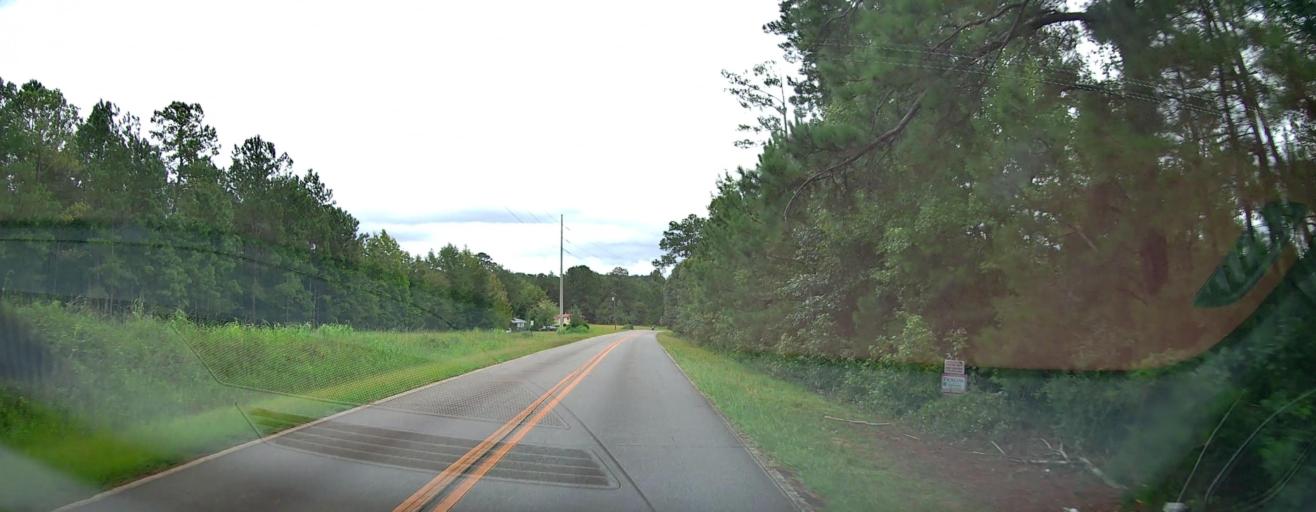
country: US
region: Georgia
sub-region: Bibb County
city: Macon
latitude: 32.7921
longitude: -83.5208
